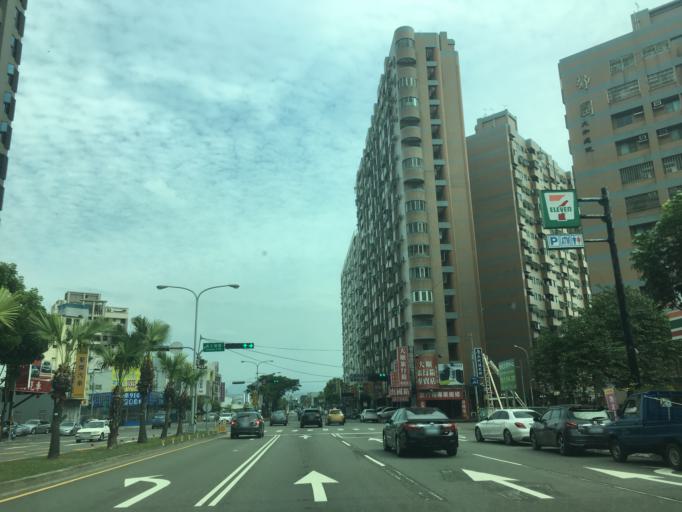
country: TW
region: Taiwan
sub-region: Taichung City
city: Taichung
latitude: 24.1114
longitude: 120.6592
